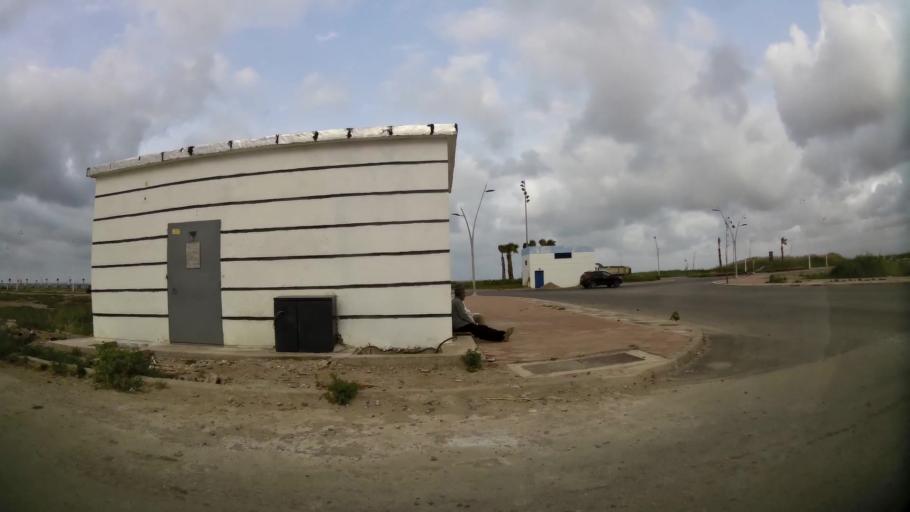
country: MA
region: Oriental
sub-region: Nador
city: Nador
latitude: 35.1573
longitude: -2.9081
